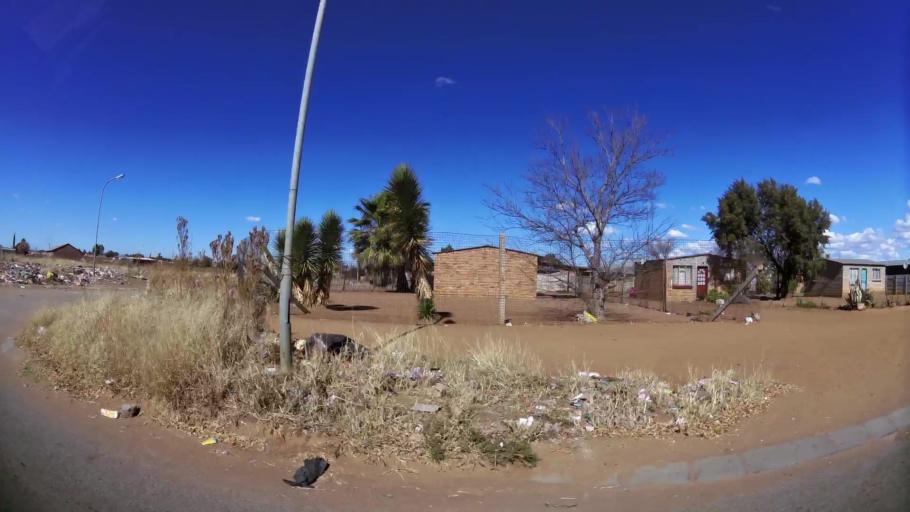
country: ZA
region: North-West
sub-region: Dr Kenneth Kaunda District Municipality
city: Klerksdorp
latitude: -26.8691
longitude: 26.5778
